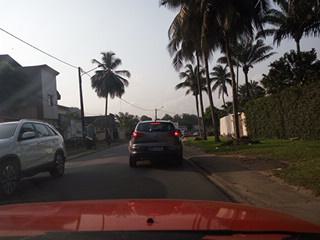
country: CI
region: Lagunes
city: Abobo
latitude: 5.3703
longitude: -3.9911
